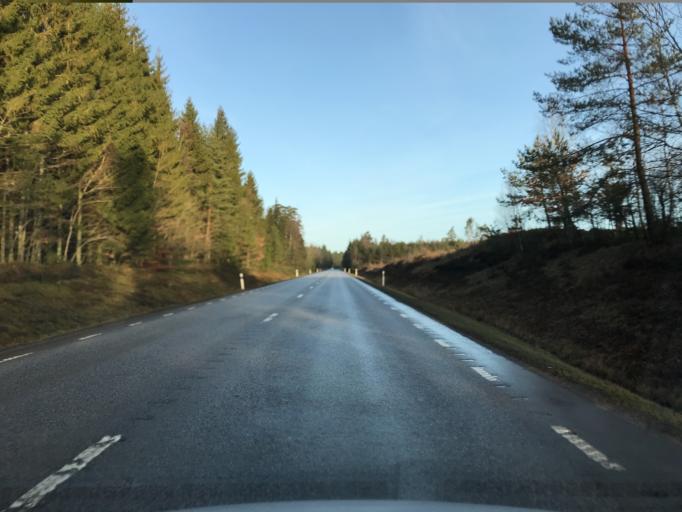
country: SE
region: Skane
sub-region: Hassleholms Kommun
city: Bjarnum
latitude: 56.2268
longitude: 13.7202
